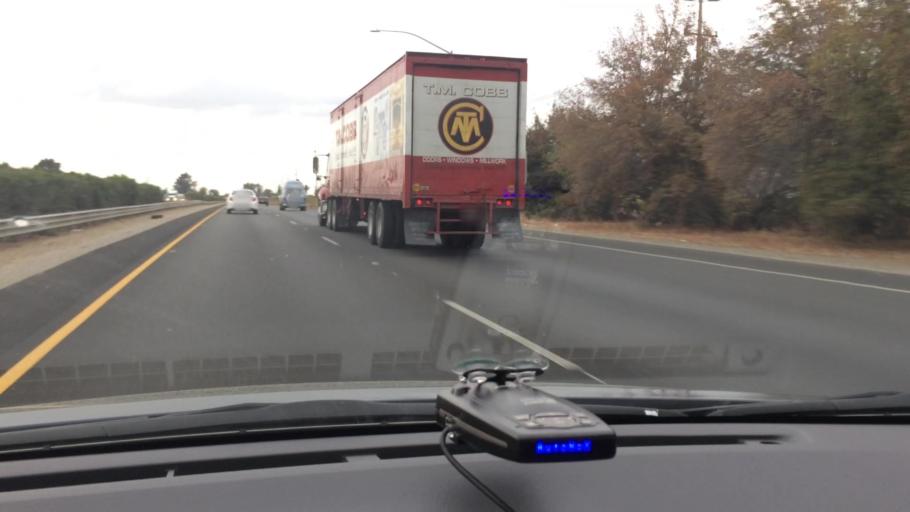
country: US
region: California
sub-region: San Joaquin County
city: Collierville
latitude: 38.1776
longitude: -121.2623
